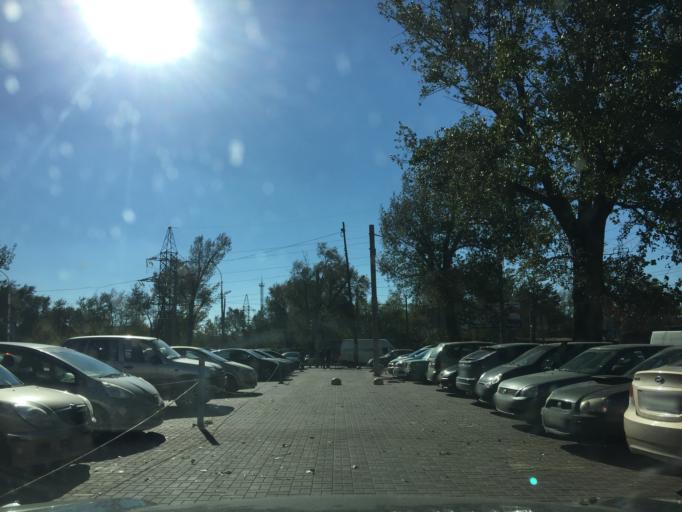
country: RU
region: Rostov
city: Imeni Chkalova
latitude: 47.2683
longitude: 39.7609
